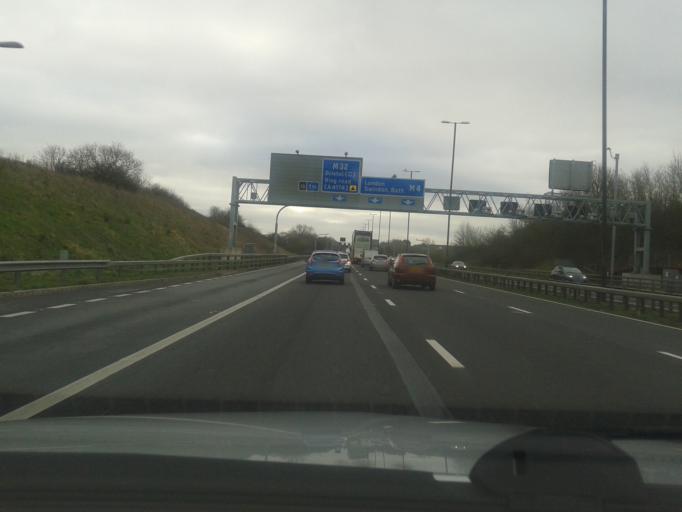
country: GB
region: England
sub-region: South Gloucestershire
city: Stoke Gifford
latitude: 51.5347
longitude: -2.5367
